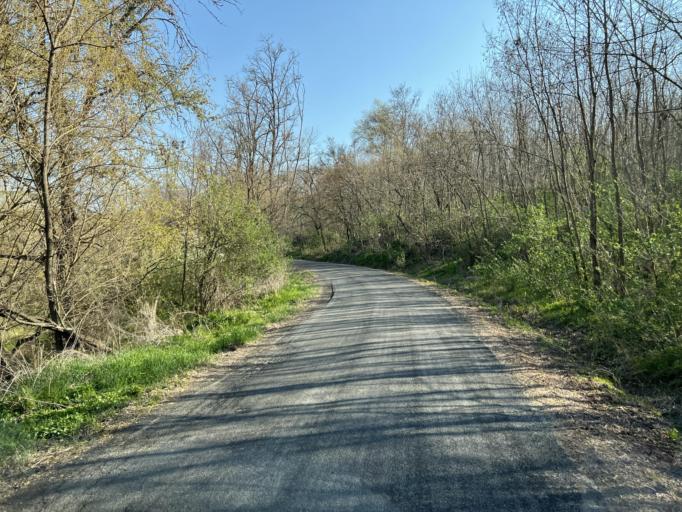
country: SK
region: Nitriansky
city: Sahy
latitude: 48.0055
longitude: 18.8212
